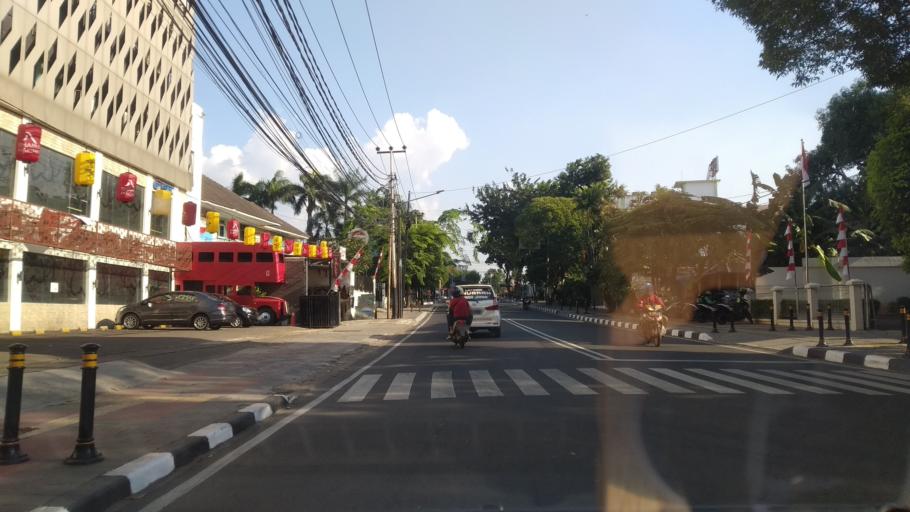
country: ID
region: Banten
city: South Tangerang
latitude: -6.2586
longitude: 106.7679
